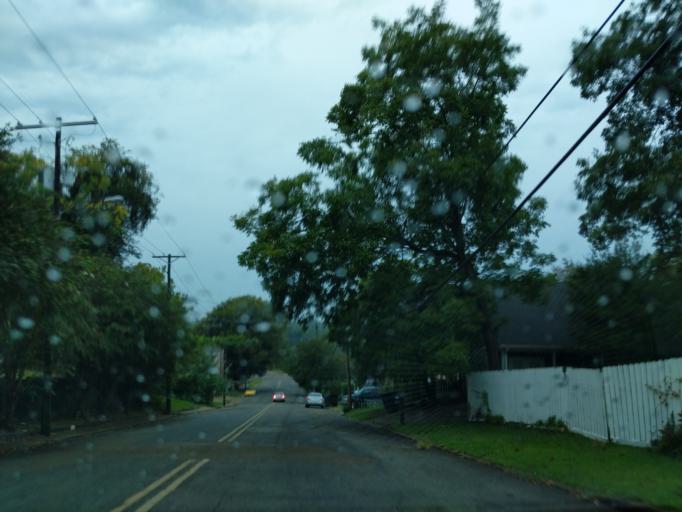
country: US
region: Mississippi
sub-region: Warren County
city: Vicksburg
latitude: 32.3548
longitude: -90.8791
